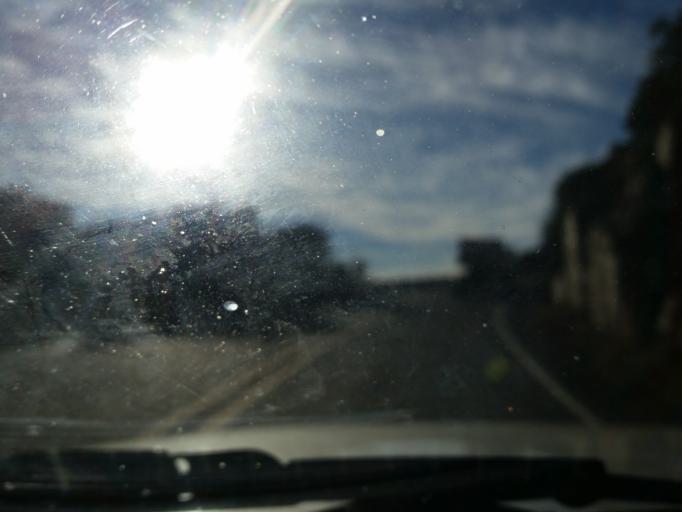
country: US
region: California
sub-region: San Bernardino County
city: Yucaipa
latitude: 34.1198
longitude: -116.9789
